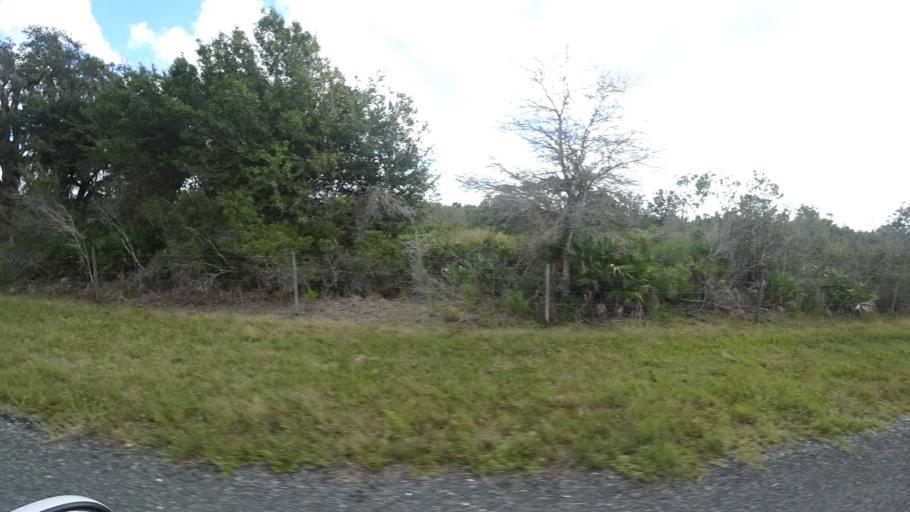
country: US
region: Florida
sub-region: Hillsborough County
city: Wimauma
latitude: 27.4799
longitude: -82.1707
